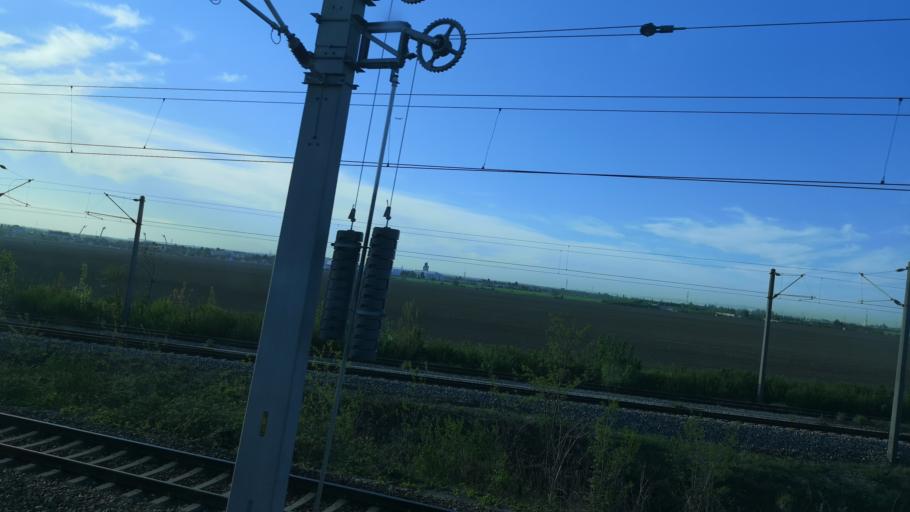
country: AT
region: Lower Austria
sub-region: Politischer Bezirk Wien-Umgebung
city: Schwechat
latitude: 48.1389
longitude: 16.4511
